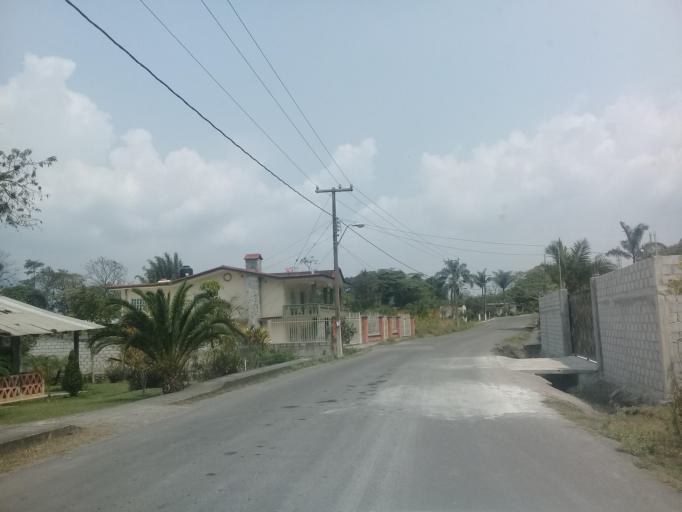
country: MX
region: Veracruz
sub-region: Ixtaczoquitlan
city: Capoluca
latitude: 18.8127
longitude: -96.9847
